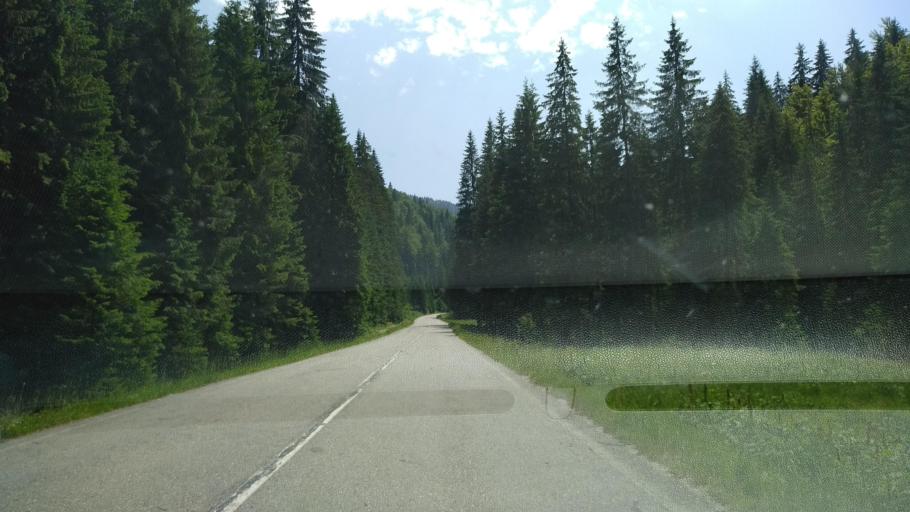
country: RO
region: Gorj
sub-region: Comuna Pades
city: Closani
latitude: 45.2619
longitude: 22.8707
